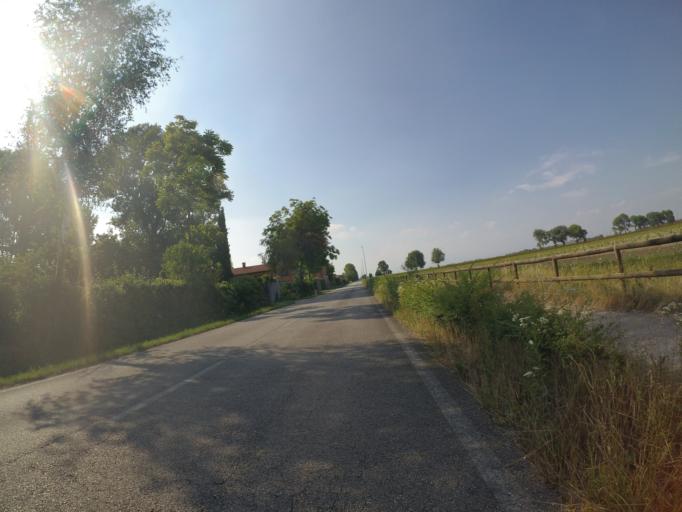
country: IT
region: Friuli Venezia Giulia
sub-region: Provincia di Udine
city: Camino al Tagliamento
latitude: 45.9289
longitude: 12.9604
